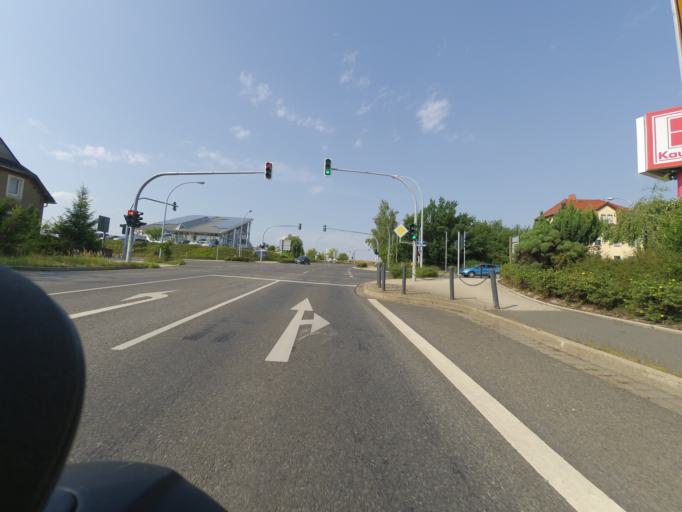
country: DE
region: Saxony
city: Waldheim
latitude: 51.0808
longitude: 12.9956
